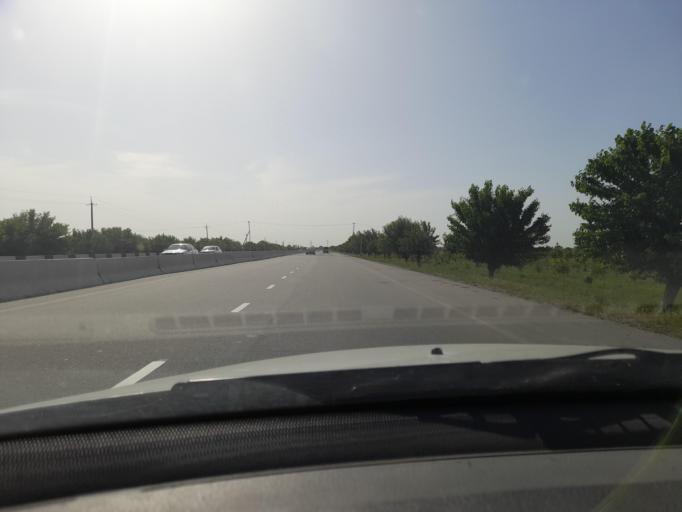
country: UZ
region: Samarqand
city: Ishtixon
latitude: 39.9572
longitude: 66.4722
